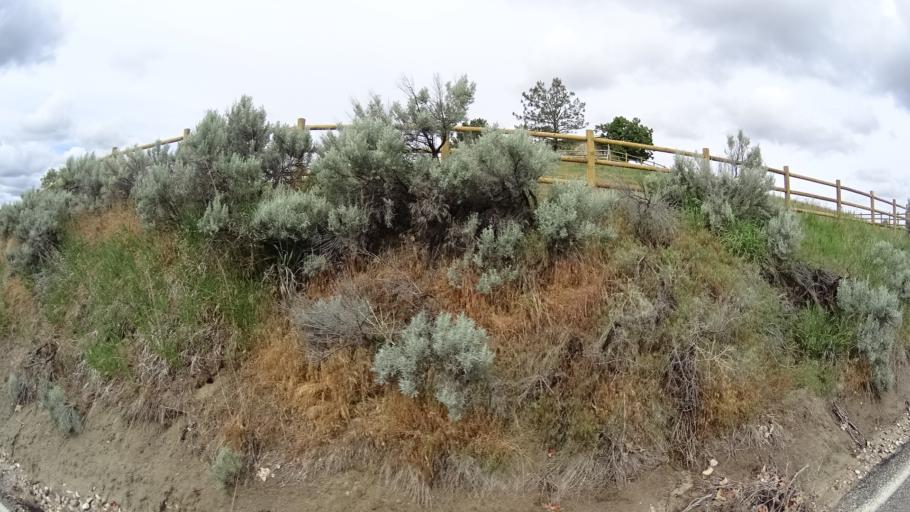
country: US
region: Idaho
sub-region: Ada County
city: Eagle
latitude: 43.7400
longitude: -116.3562
